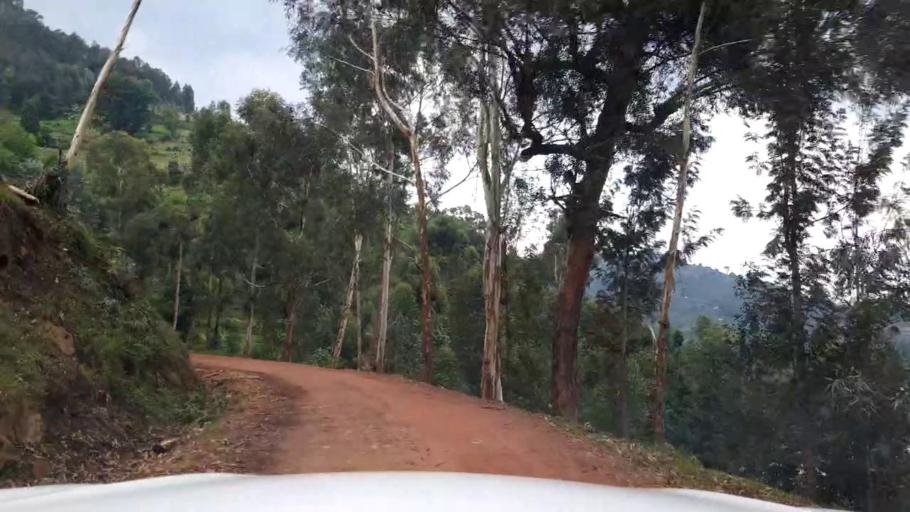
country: UG
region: Western Region
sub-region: Kisoro District
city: Kisoro
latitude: -1.3859
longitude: 29.7981
